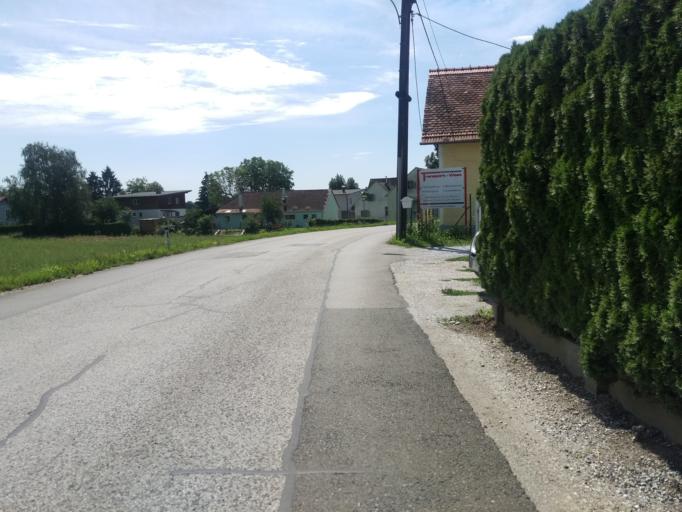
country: AT
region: Styria
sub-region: Politischer Bezirk Graz-Umgebung
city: Feldkirchen bei Graz
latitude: 47.0213
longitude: 15.4435
